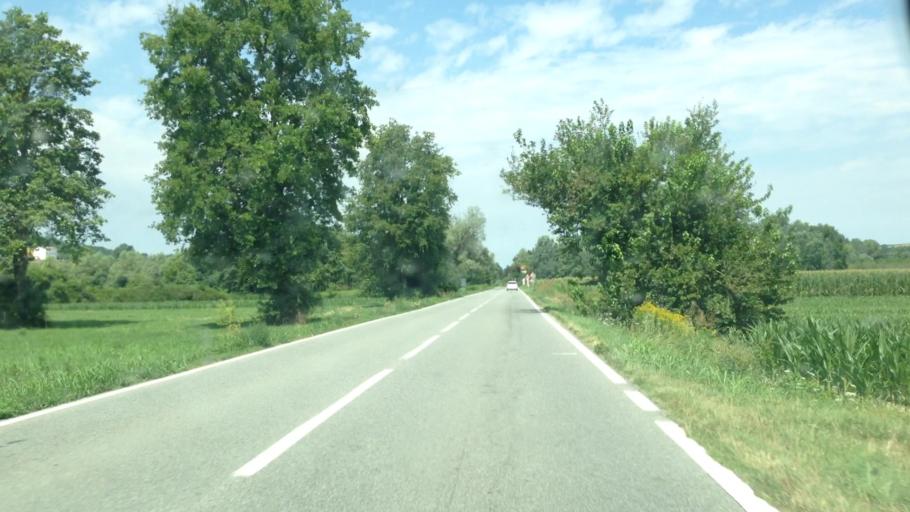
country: IT
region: Piedmont
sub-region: Provincia di Asti
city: Castell'Alfero
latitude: 44.9900
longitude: 8.2205
